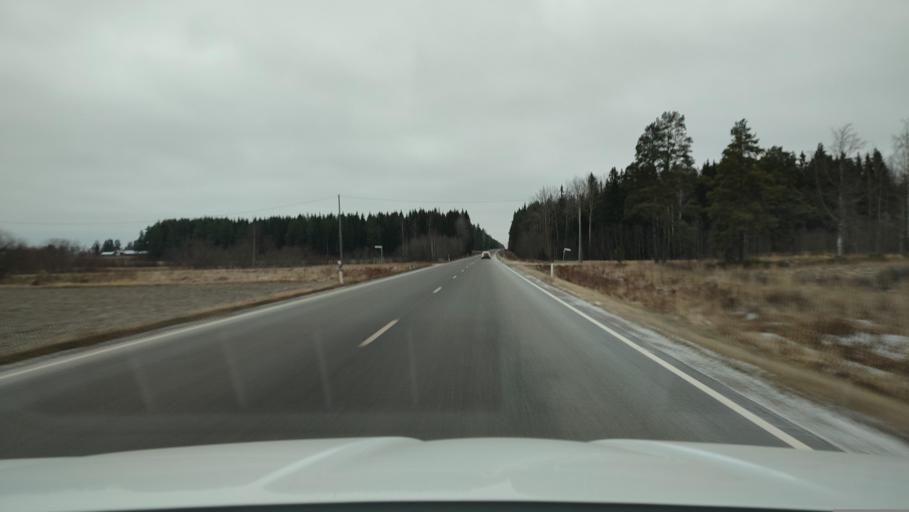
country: FI
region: Ostrobothnia
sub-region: Sydosterbotten
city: Naerpes
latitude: 62.5477
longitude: 21.4707
